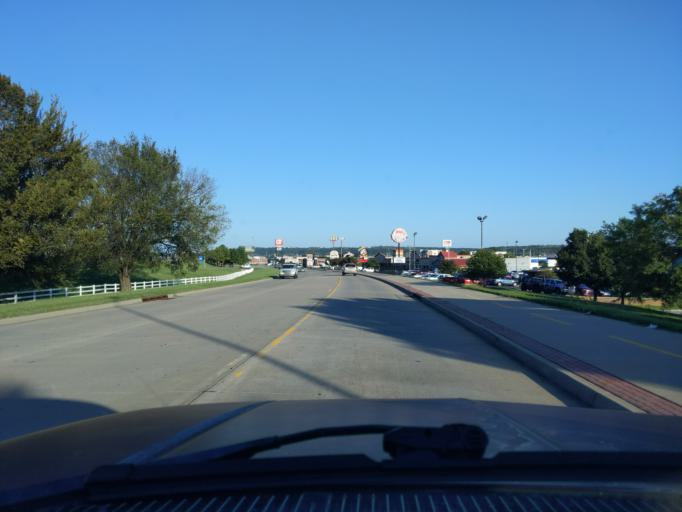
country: US
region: Oklahoma
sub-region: Tulsa County
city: Sand Springs
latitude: 36.1366
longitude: -96.1198
